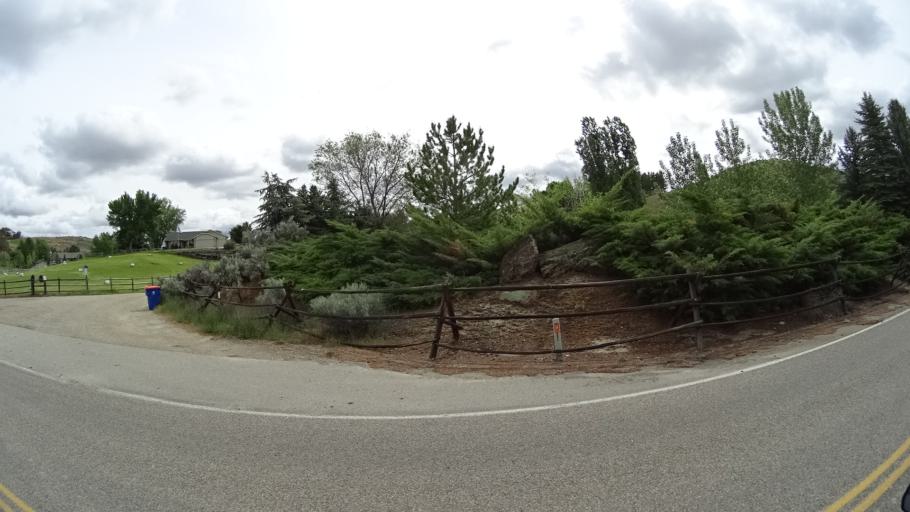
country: US
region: Idaho
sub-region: Ada County
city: Eagle
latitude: 43.7365
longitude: -116.3574
